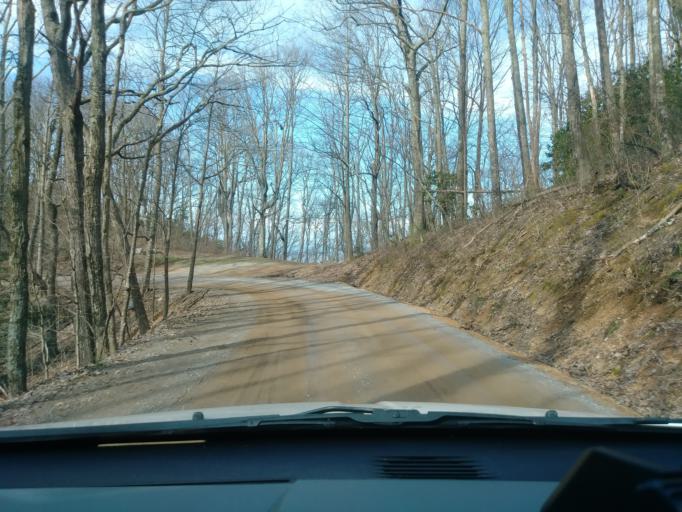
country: US
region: Tennessee
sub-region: Greene County
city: Tusculum
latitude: 36.0315
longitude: -82.7205
